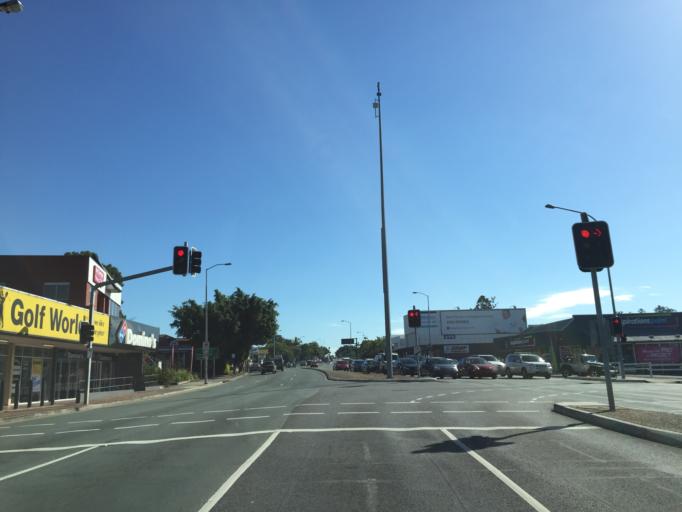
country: AU
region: Queensland
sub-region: Brisbane
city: Wilston
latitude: -27.4372
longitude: 153.0069
